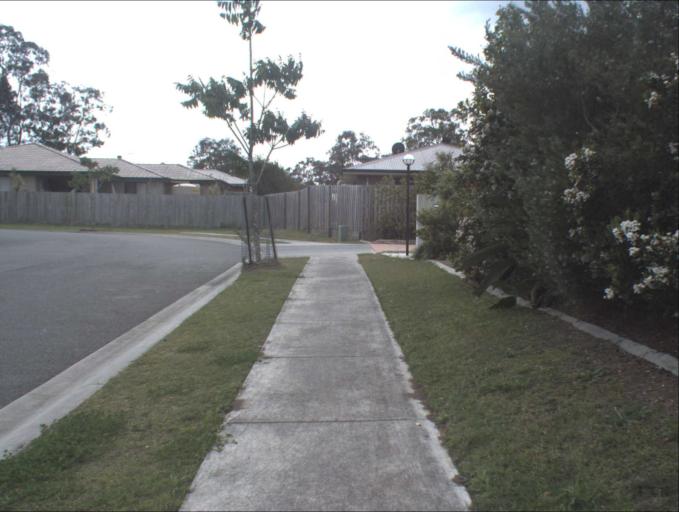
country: AU
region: Queensland
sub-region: Logan
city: Waterford West
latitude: -27.6850
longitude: 153.1365
